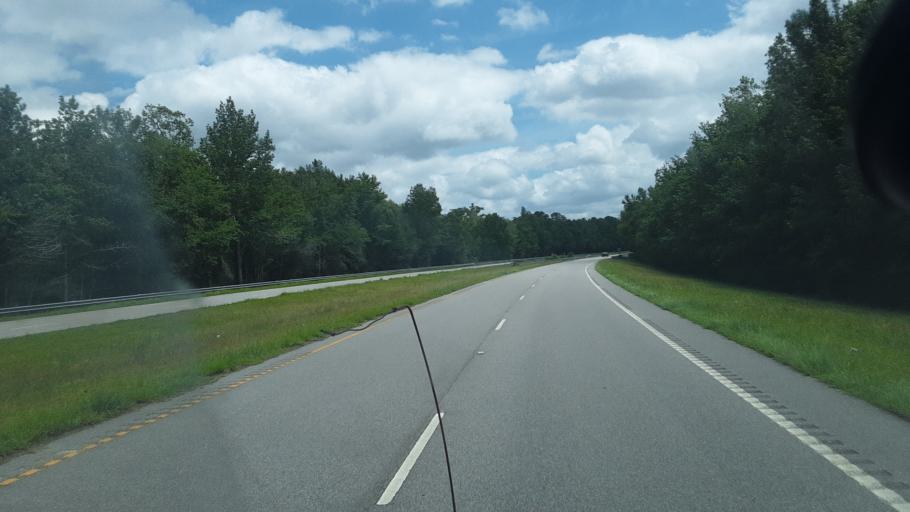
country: US
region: North Carolina
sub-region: Columbus County
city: Tabor City
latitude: 34.1176
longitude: -78.9705
